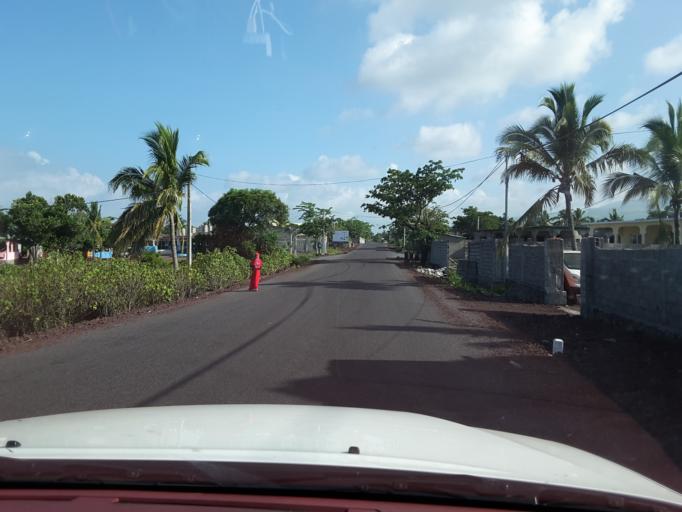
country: KM
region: Grande Comore
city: Oussivo
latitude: -11.5563
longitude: 43.2736
